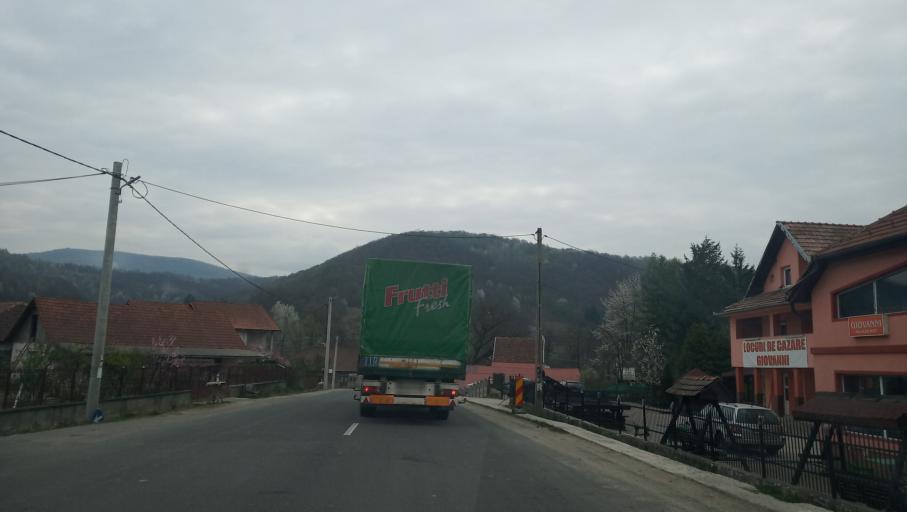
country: RO
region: Arad
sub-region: Comuna Varfurile
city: Varfurile
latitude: 46.3427
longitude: 22.5565
